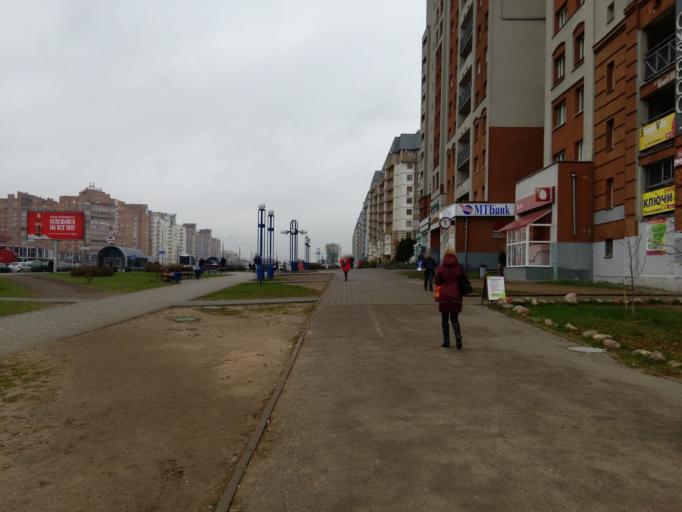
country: BY
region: Minsk
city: Borovlyany
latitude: 53.9439
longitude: 27.6856
